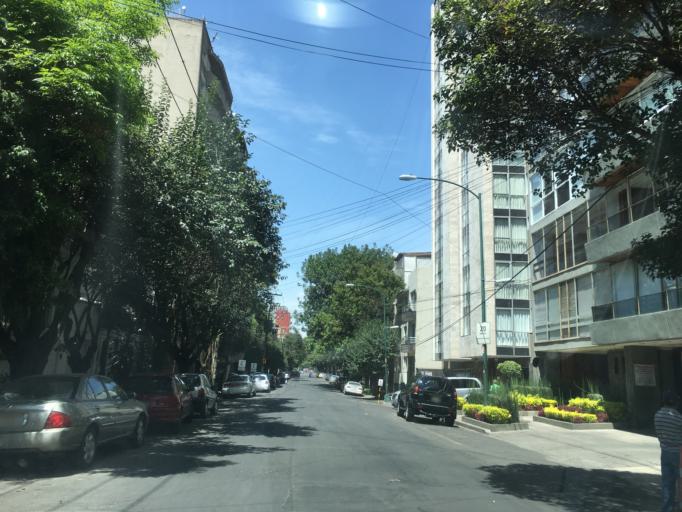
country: MX
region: Mexico City
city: Colonia del Valle
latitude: 19.3945
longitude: -99.1704
